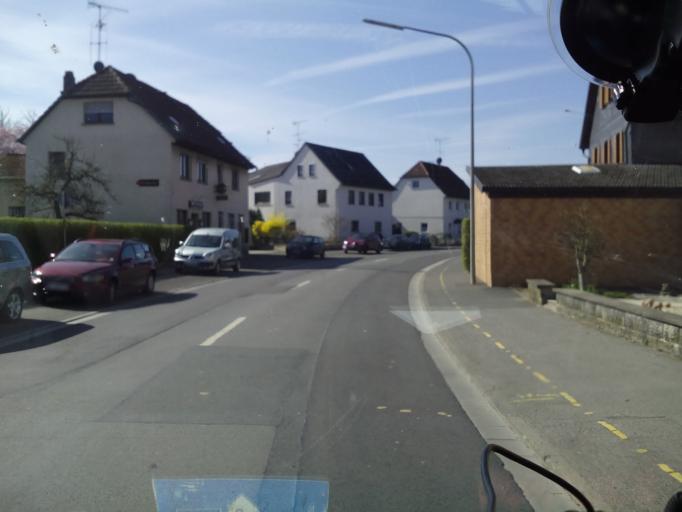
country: DE
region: Bavaria
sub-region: Upper Franconia
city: Michelau
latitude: 50.1652
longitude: 11.1132
